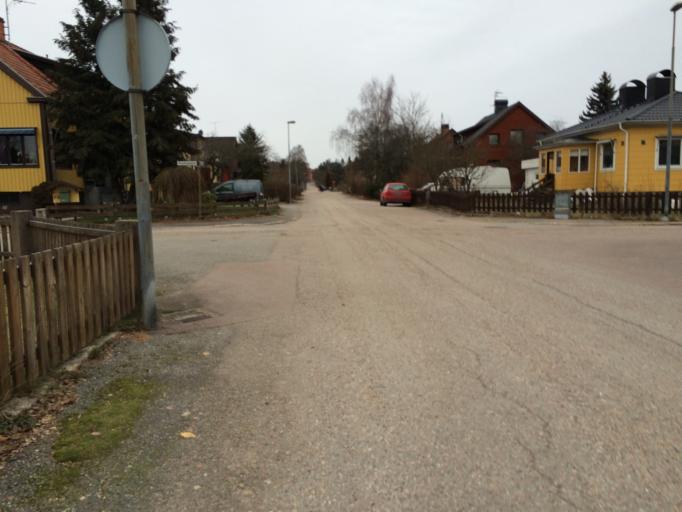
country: SE
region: Vaestmanland
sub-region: Hallstahammars Kommun
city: Hallstahammar
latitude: 59.6160
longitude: 16.2360
